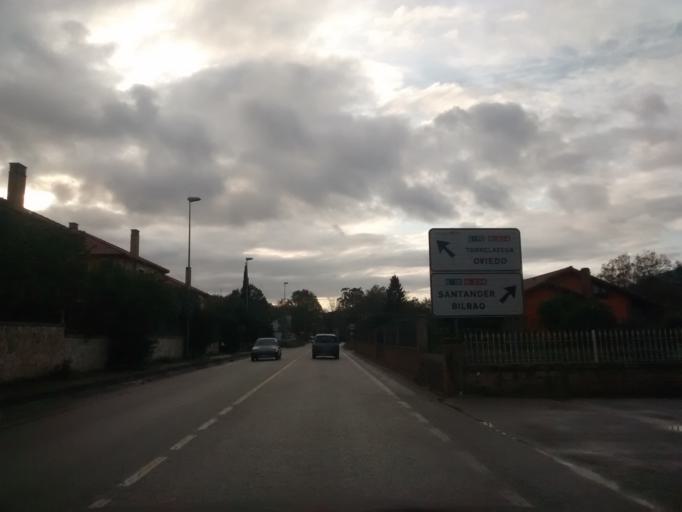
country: ES
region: Cantabria
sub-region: Provincia de Cantabria
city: Lierganes
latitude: 43.3564
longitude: -3.7706
